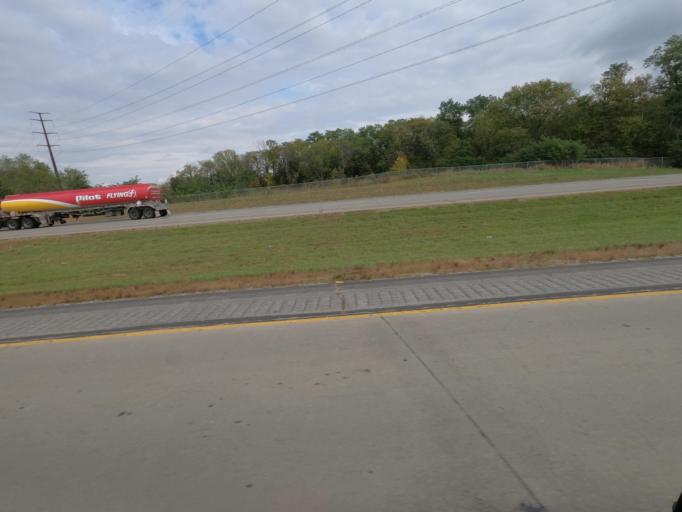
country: US
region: Iowa
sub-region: Polk County
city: Altoona
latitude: 41.6276
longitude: -93.4990
